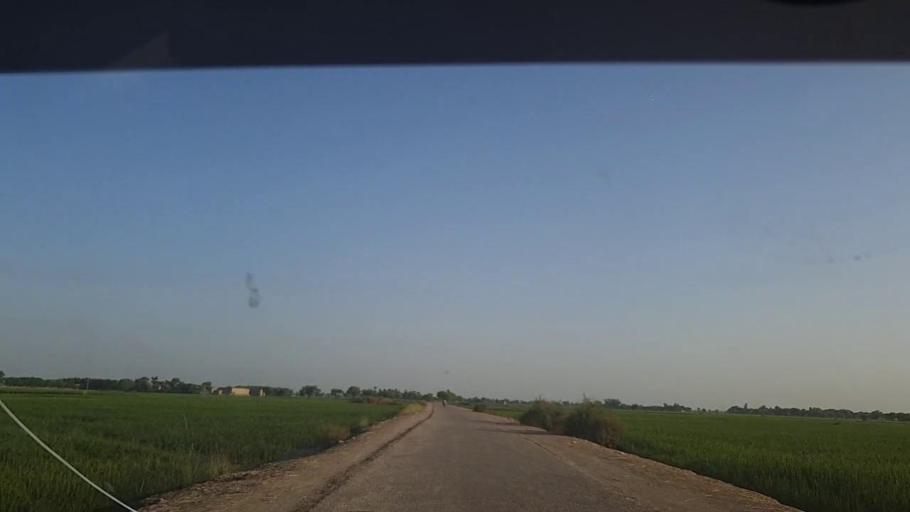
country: PK
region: Sindh
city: Thul
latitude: 28.2142
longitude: 68.8695
